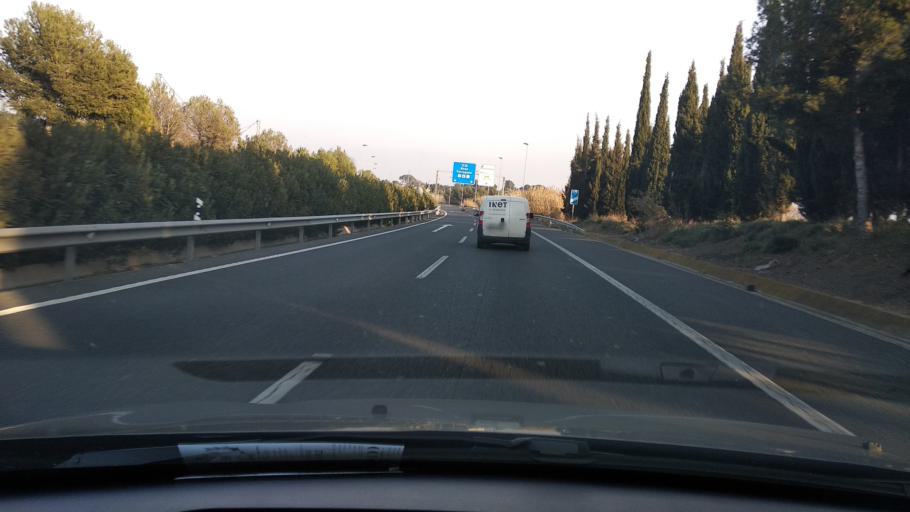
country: ES
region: Catalonia
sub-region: Provincia de Tarragona
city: Reus
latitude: 41.1300
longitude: 1.1122
